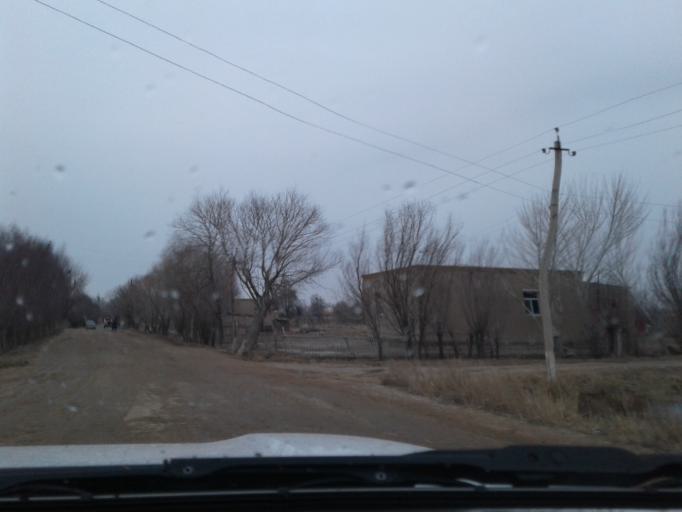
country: UZ
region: Karakalpakstan
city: Shumanay Shahri
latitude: 42.2776
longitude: 58.6538
